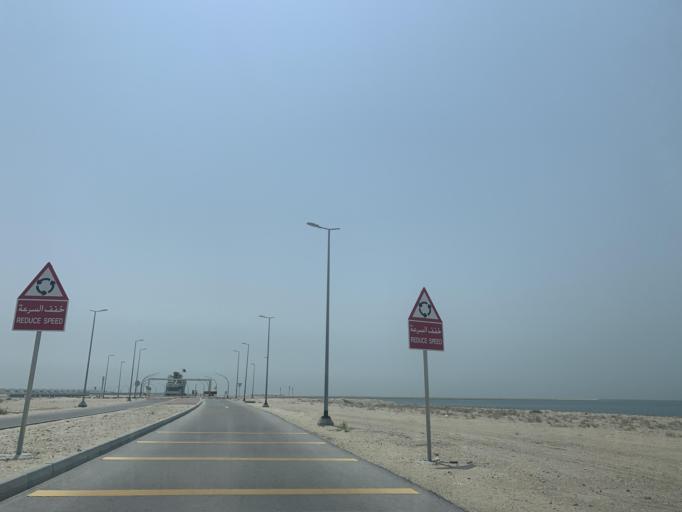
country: BH
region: Central Governorate
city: Dar Kulayb
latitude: 25.8310
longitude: 50.5949
